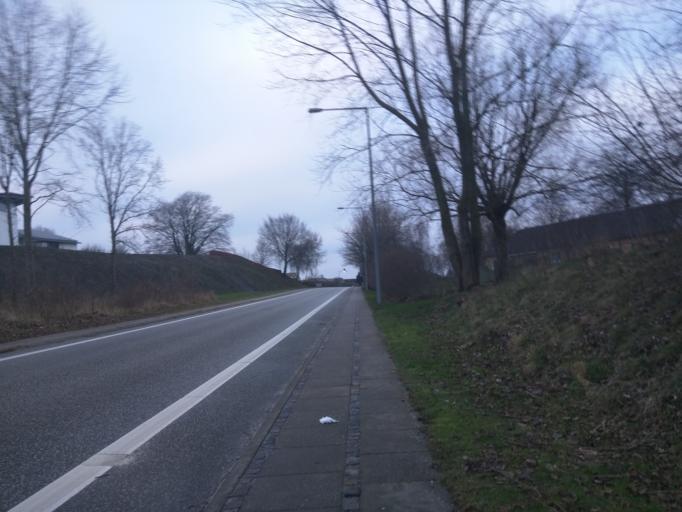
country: DK
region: South Denmark
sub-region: Fredericia Kommune
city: Snoghoj
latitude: 55.5292
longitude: 9.7313
